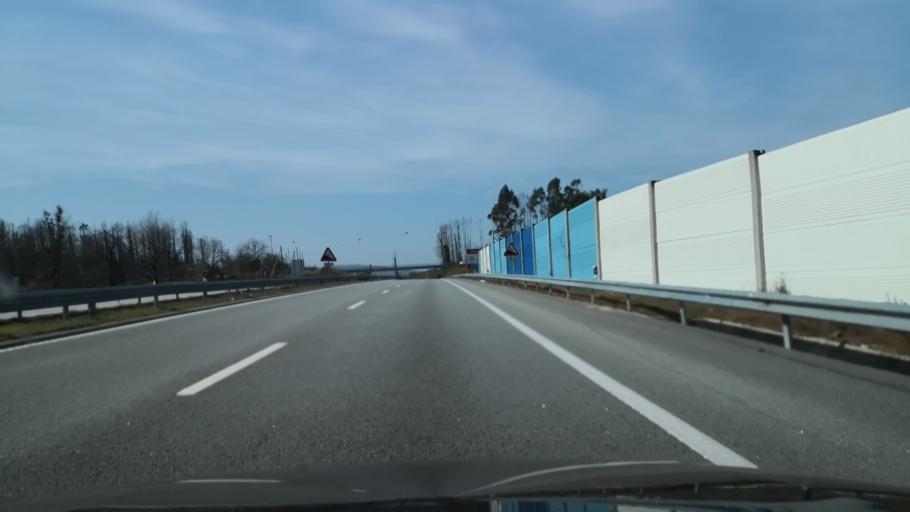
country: PT
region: Viseu
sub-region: Oliveira de Frades
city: Oliveira de Frades
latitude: 40.6818
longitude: -8.1830
